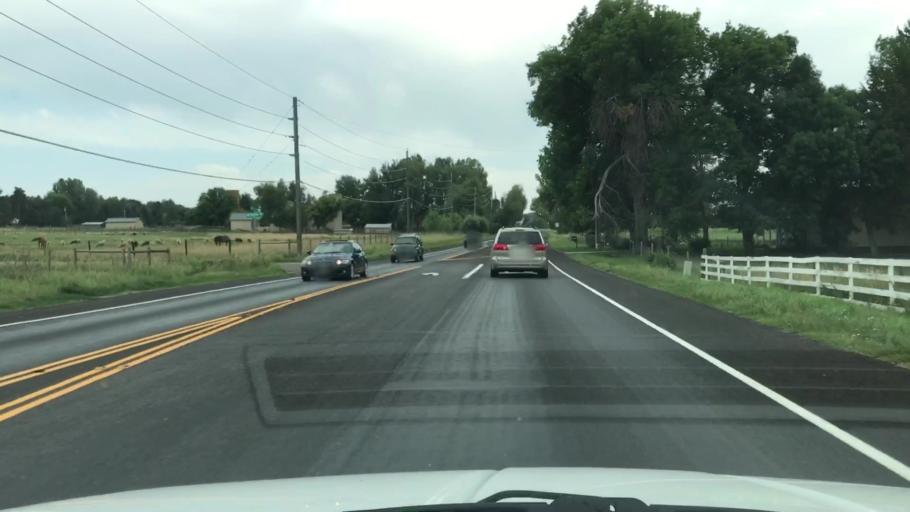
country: US
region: Colorado
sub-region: Boulder County
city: Louisville
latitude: 40.0077
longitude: -105.1782
